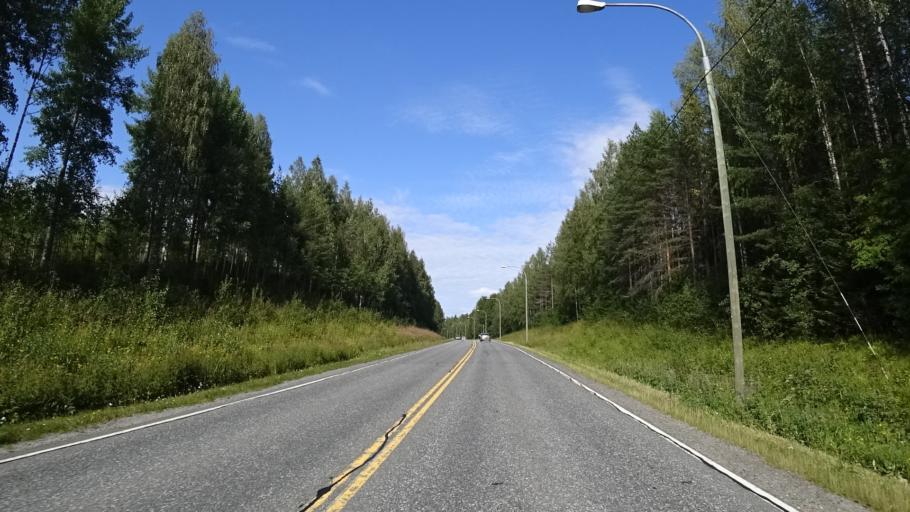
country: FI
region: North Karelia
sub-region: Joensuu
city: Eno
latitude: 62.7819
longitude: 30.0742
